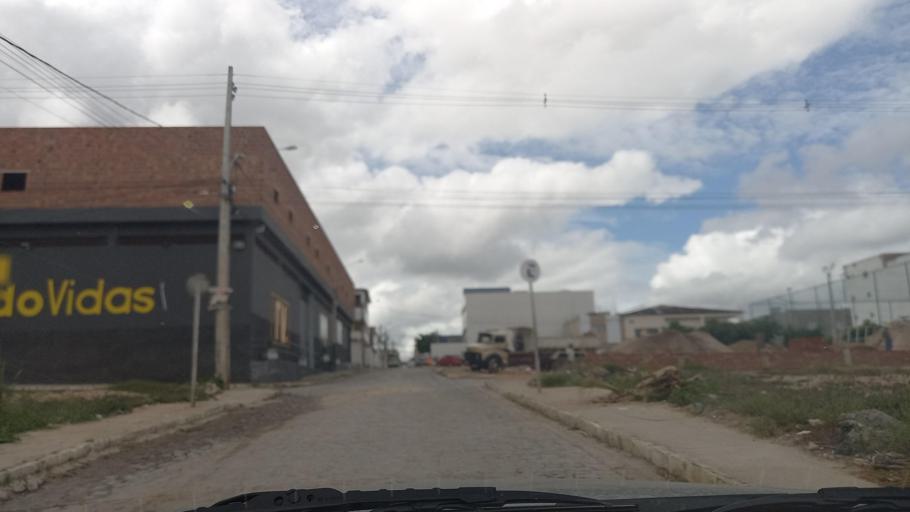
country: BR
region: Pernambuco
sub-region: Caruaru
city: Caruaru
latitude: -8.2672
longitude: -35.9595
